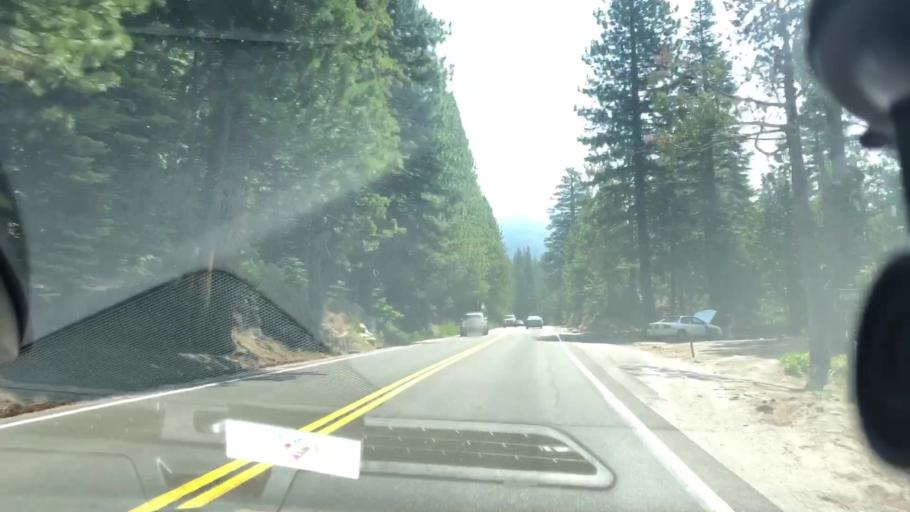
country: US
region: California
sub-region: El Dorado County
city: South Lake Tahoe
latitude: 38.7894
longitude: -120.1702
